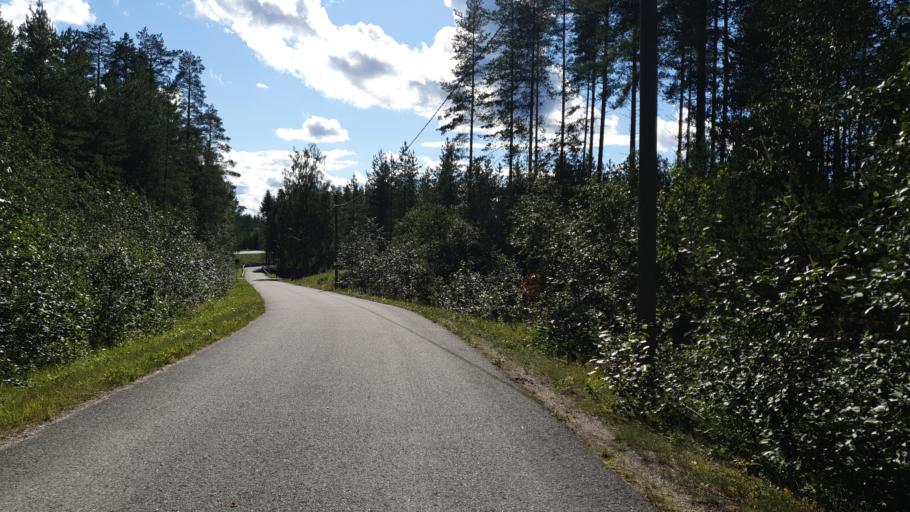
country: FI
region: Kainuu
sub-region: Kehys-Kainuu
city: Kuhmo
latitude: 64.0944
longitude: 29.4613
